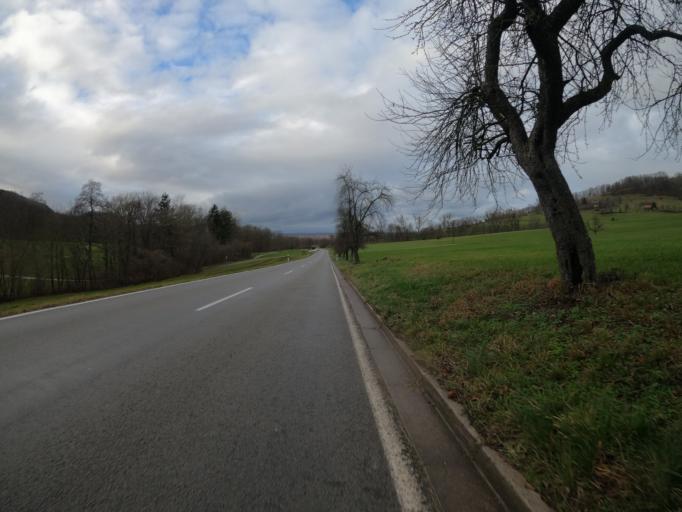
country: DE
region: Baden-Wuerttemberg
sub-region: Regierungsbezirk Stuttgart
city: Waldstetten
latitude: 48.7517
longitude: 9.8357
